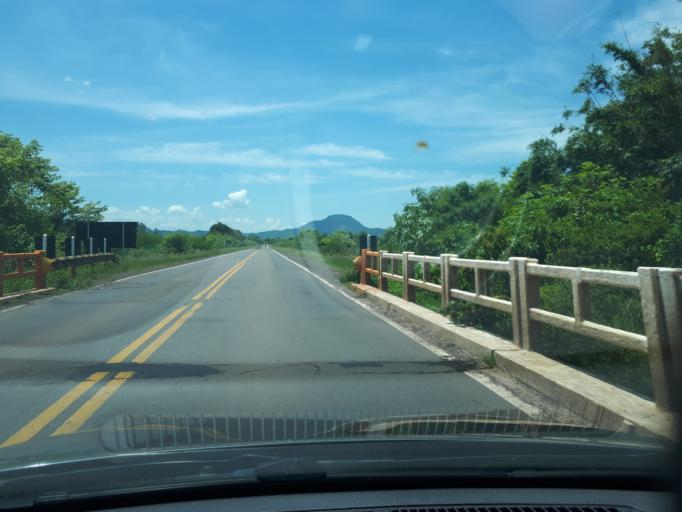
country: BR
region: Rio Grande do Sul
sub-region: Candelaria
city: Candelaria
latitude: -29.7272
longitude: -52.9346
